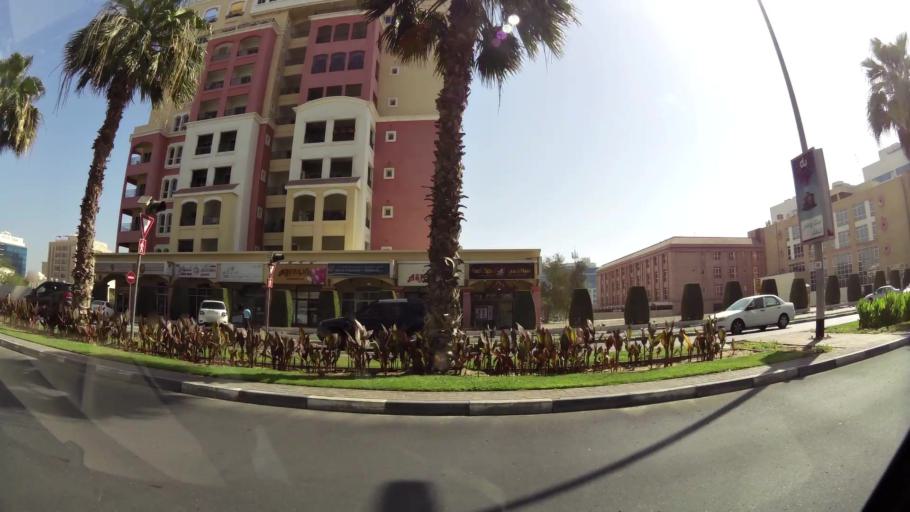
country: AE
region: Ash Shariqah
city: Sharjah
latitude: 25.2525
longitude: 55.2877
